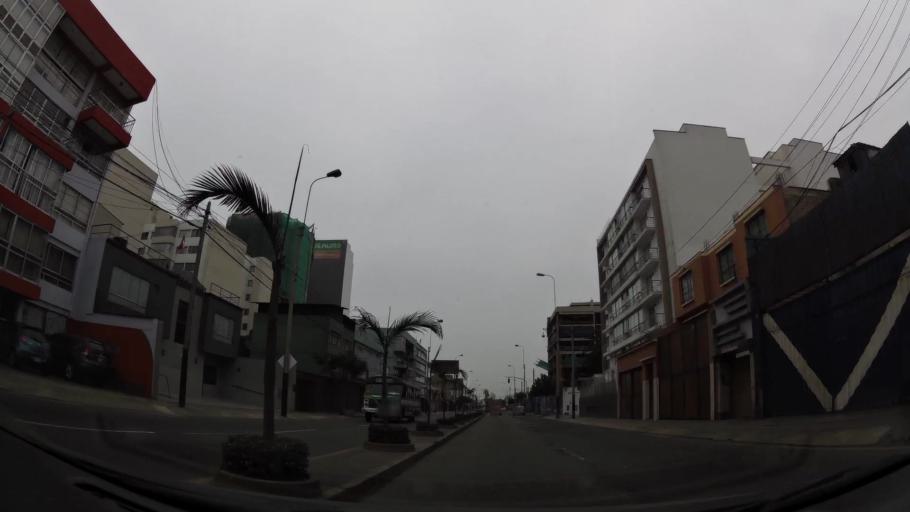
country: PE
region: Lima
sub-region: Lima
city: San Isidro
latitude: -12.1122
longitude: -77.0494
